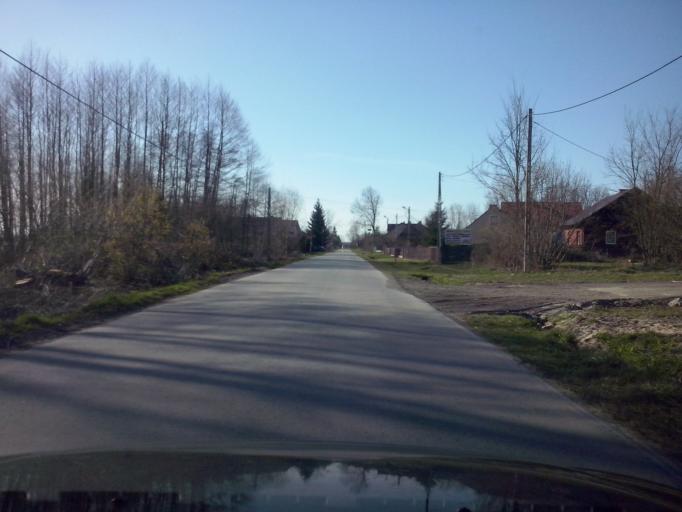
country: PL
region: Subcarpathian Voivodeship
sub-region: Powiat nizanski
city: Krzeszow
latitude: 50.3791
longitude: 22.3918
